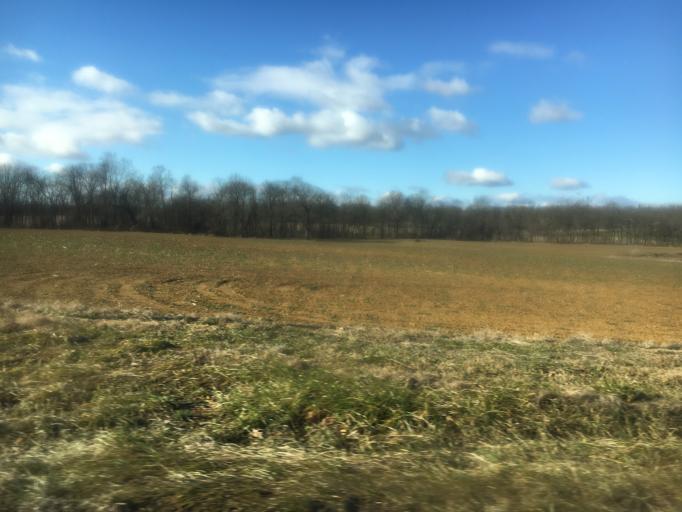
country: US
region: Pennsylvania
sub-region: Lehigh County
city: Egypt
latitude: 40.6555
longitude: -75.5529
